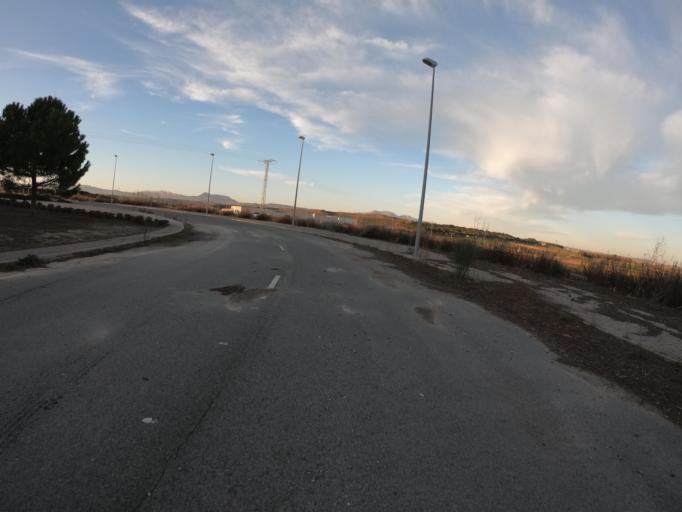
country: ES
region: Basque Country
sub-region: Provincia de Alava
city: Oyon
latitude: 42.4863
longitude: -2.4158
